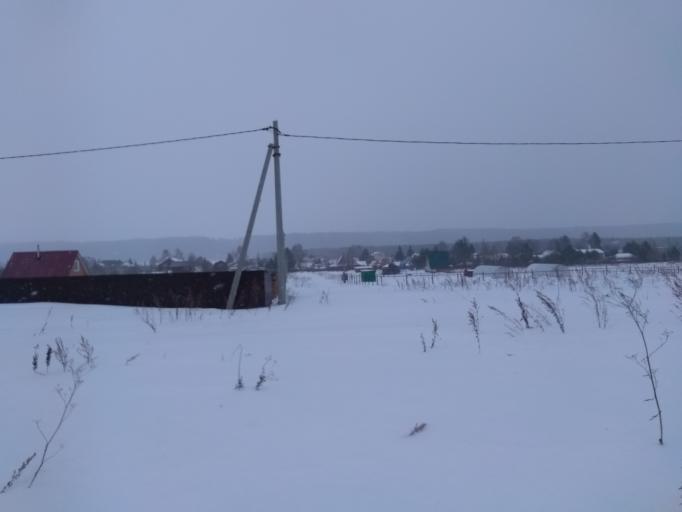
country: RU
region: Perm
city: Sylva
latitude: 57.8449
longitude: 56.7870
